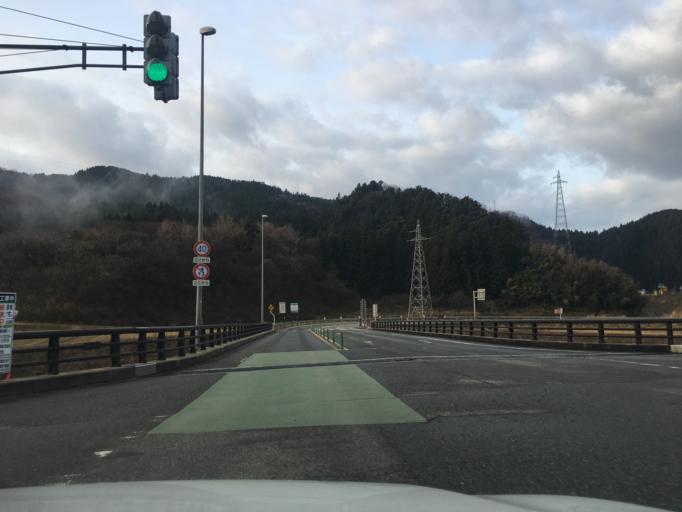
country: JP
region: Yamagata
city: Tsuruoka
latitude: 38.6053
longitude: 139.5880
